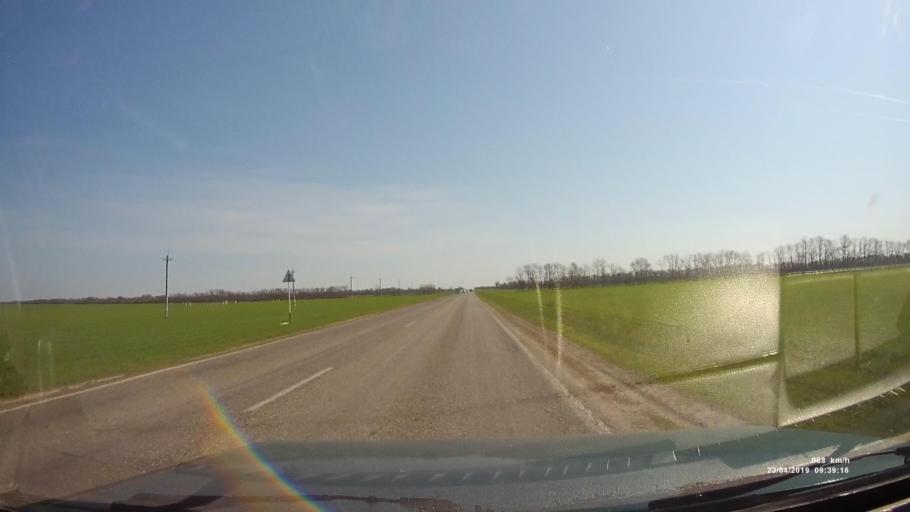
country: RU
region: Rostov
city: Gundorovskiy
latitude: 46.8529
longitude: 41.9225
